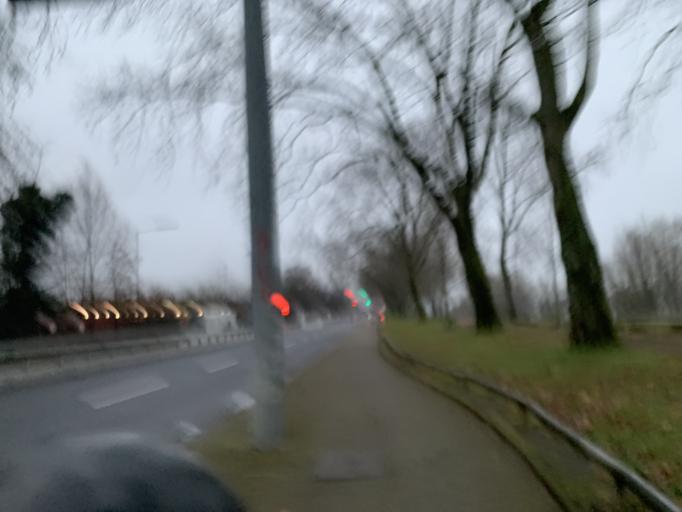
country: DE
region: North Rhine-Westphalia
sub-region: Regierungsbezirk Dusseldorf
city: Dusseldorf
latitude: 51.2576
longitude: 6.7343
